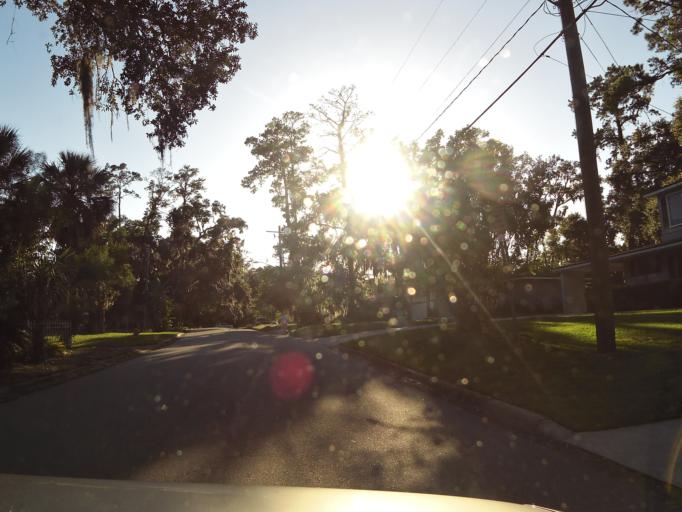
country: US
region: Florida
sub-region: Duval County
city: Jacksonville
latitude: 30.2644
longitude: -81.6453
